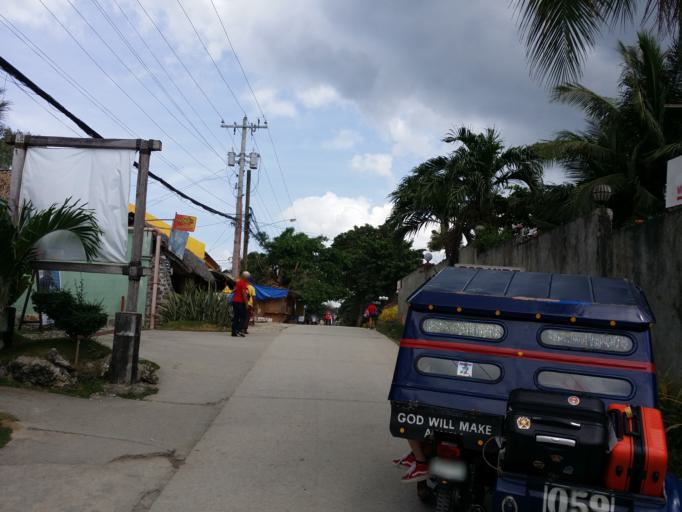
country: PH
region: Central Visayas
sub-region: Province of Bohol
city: Tawala
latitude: 9.5489
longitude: 123.7721
